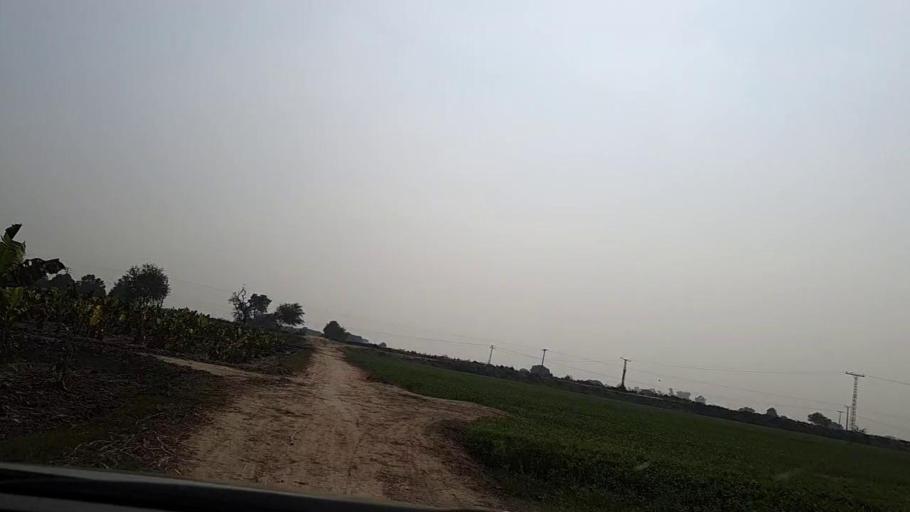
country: PK
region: Sindh
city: Sakrand
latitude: 26.1406
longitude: 68.2340
